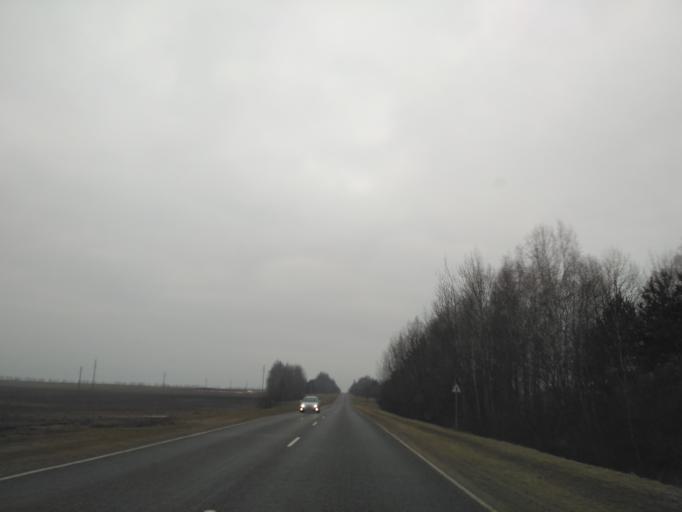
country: BY
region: Minsk
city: Haradzyeya
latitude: 53.3268
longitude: 26.4492
